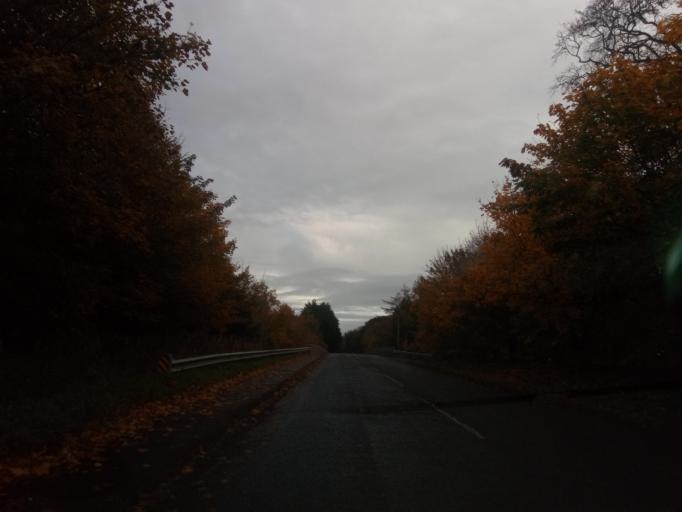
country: GB
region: Scotland
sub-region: The Scottish Borders
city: Eyemouth
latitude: 55.8476
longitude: -2.1165
